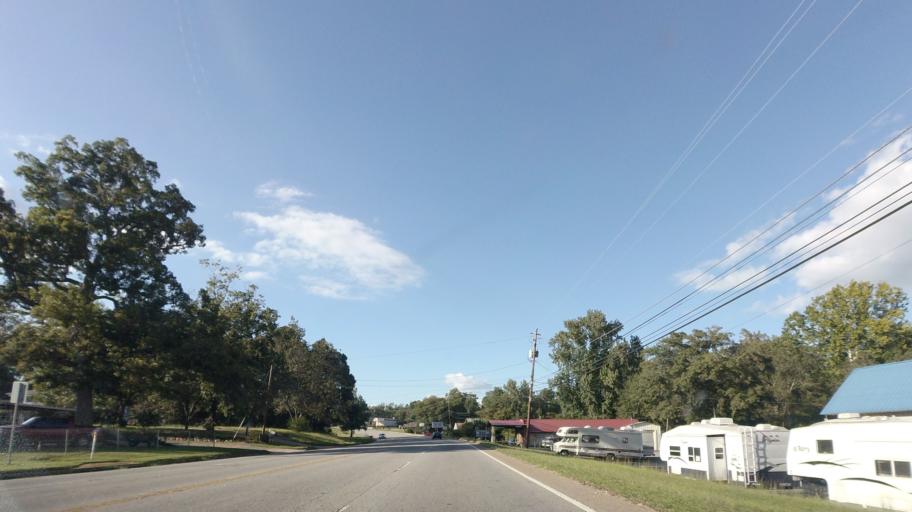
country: US
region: Georgia
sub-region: Upson County
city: Hannahs Mill
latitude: 32.9410
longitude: -84.3339
